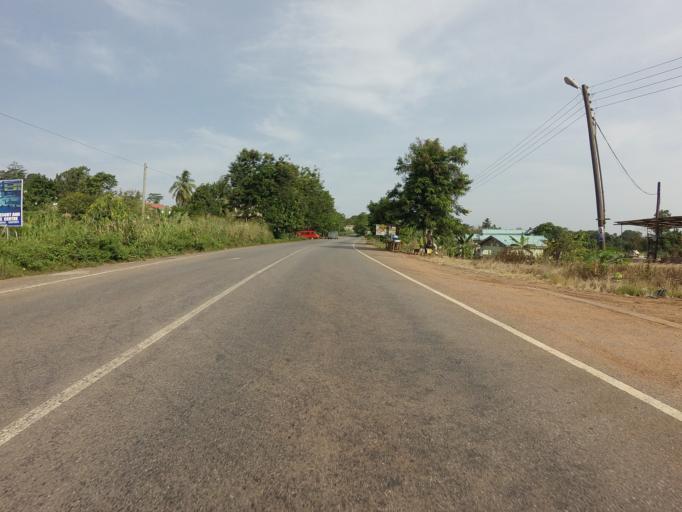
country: GH
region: Eastern
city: Aburi
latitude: 5.8835
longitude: -0.1553
